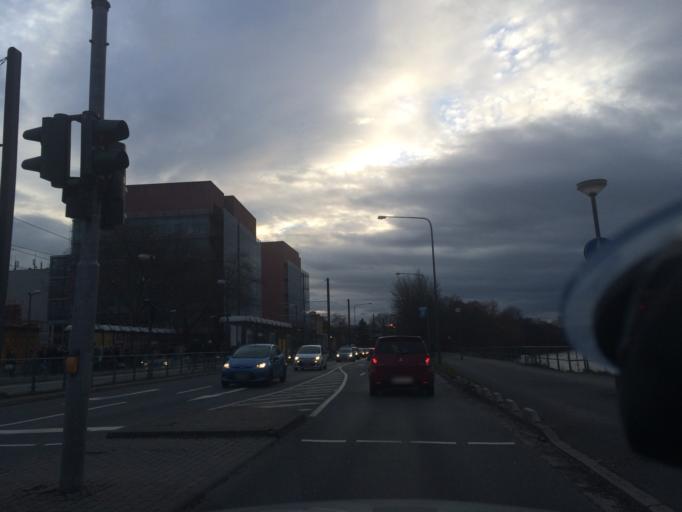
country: DE
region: Hesse
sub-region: Regierungsbezirk Darmstadt
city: Frankfurt am Main
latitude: 50.0966
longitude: 8.6605
